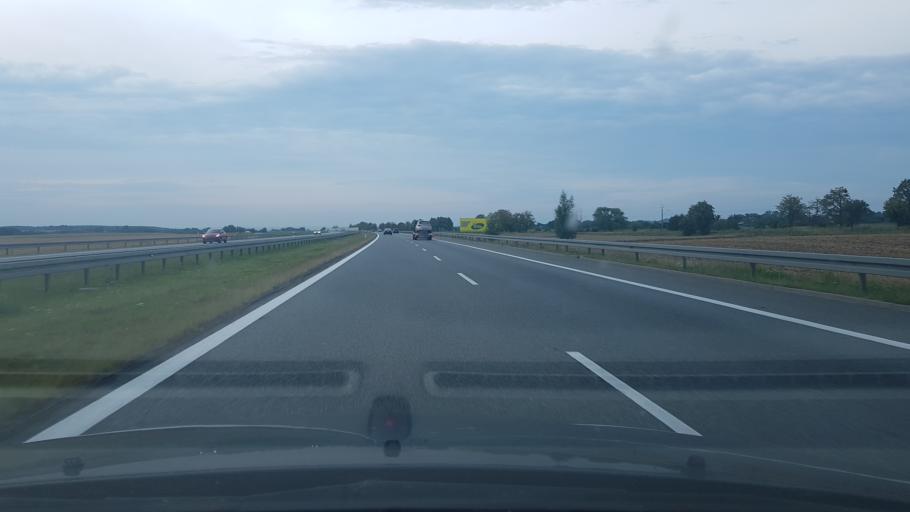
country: PL
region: Warmian-Masurian Voivodeship
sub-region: Powiat ostrodzki
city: Maldyty
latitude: 53.9857
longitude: 19.6956
